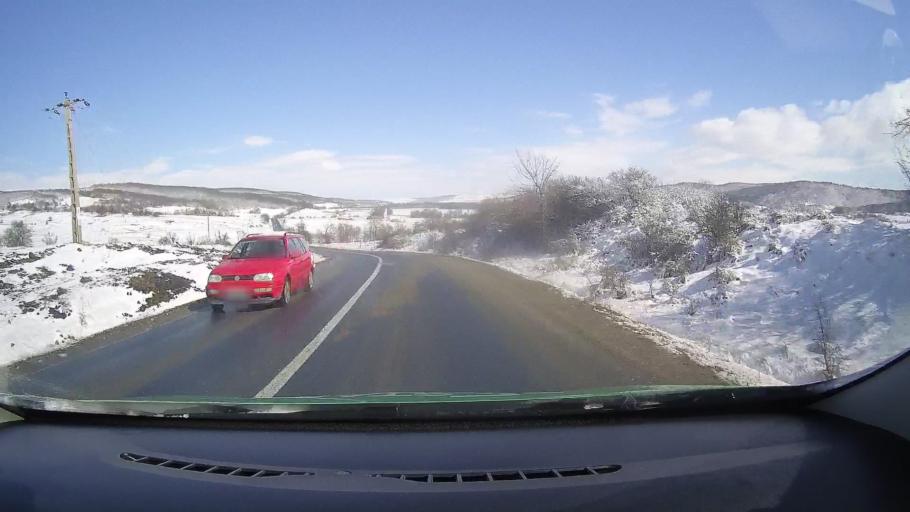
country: RO
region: Sibiu
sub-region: Comuna Rosia
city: Rosia
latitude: 45.8195
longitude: 24.3791
